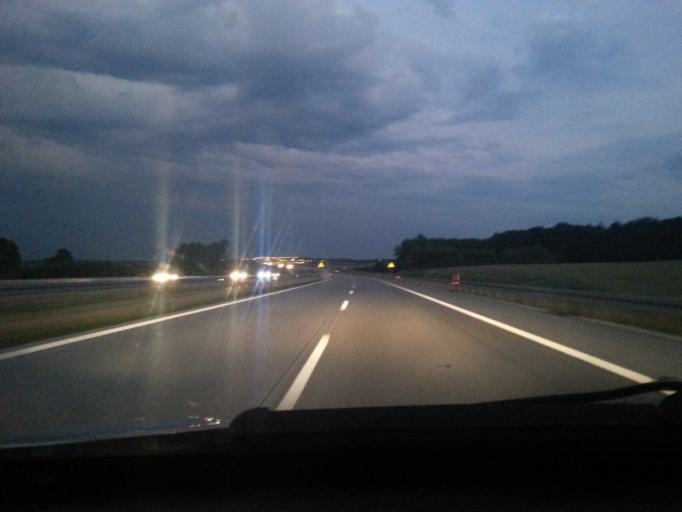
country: PL
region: Lodz Voivodeship
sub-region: Powiat sieradzki
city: Sieradz
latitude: 51.5417
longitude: 18.6986
